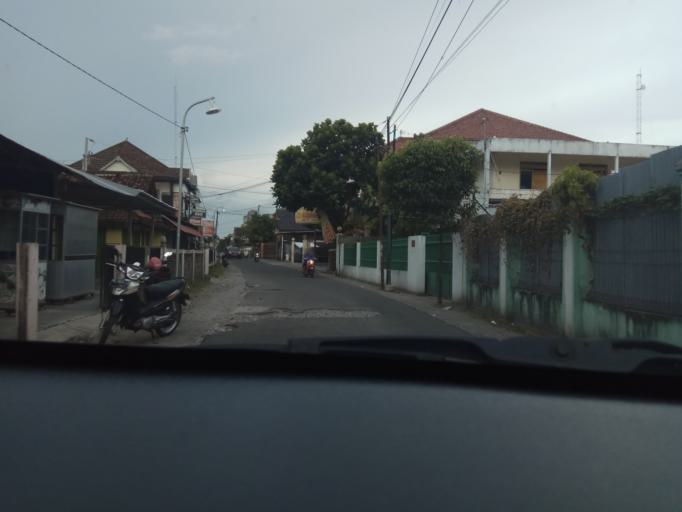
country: ID
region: Daerah Istimewa Yogyakarta
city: Depok
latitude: -7.7620
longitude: 110.3951
